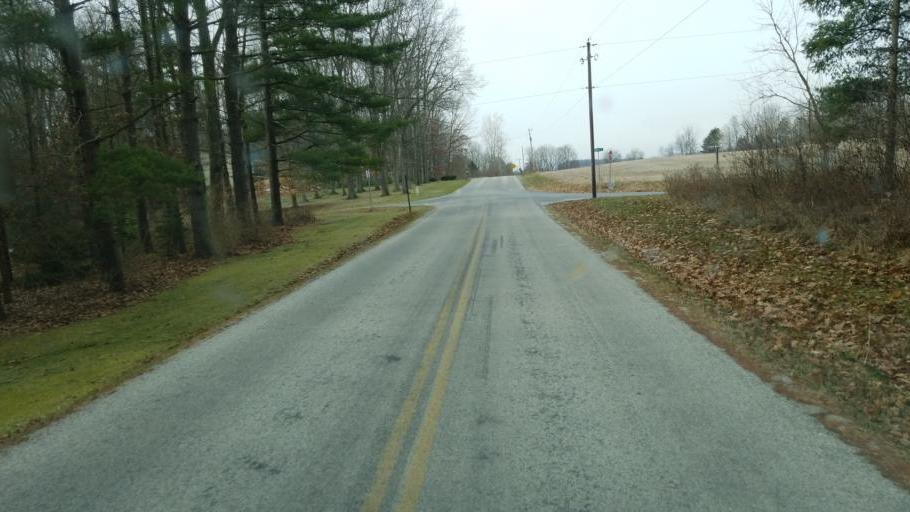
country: US
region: Ohio
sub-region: Sandusky County
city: Bellville
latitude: 40.6309
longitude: -82.5531
